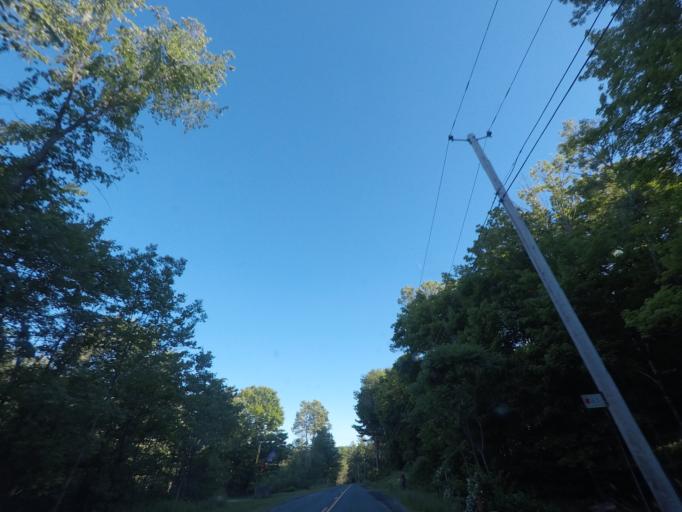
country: US
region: New York
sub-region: Rensselaer County
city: Averill Park
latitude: 42.5694
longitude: -73.5326
